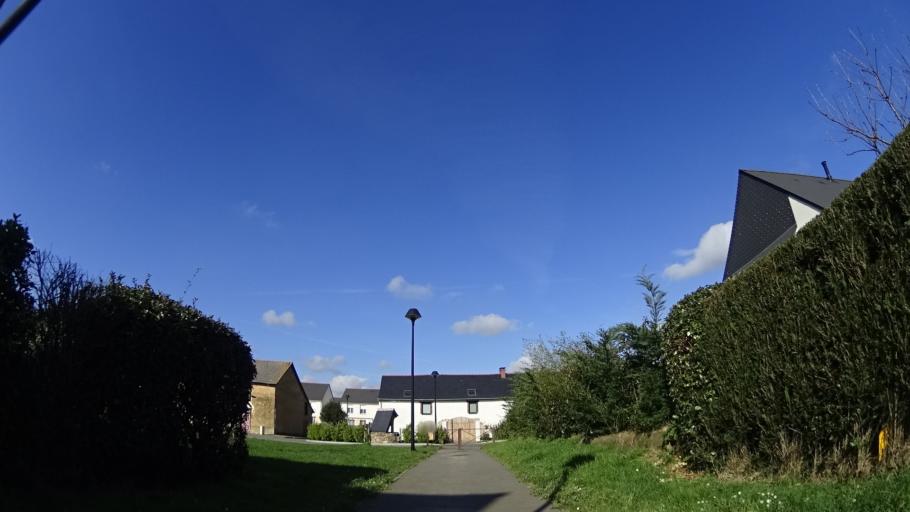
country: FR
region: Brittany
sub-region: Departement d'Ille-et-Vilaine
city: Geveze
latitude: 48.2242
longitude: -1.7990
